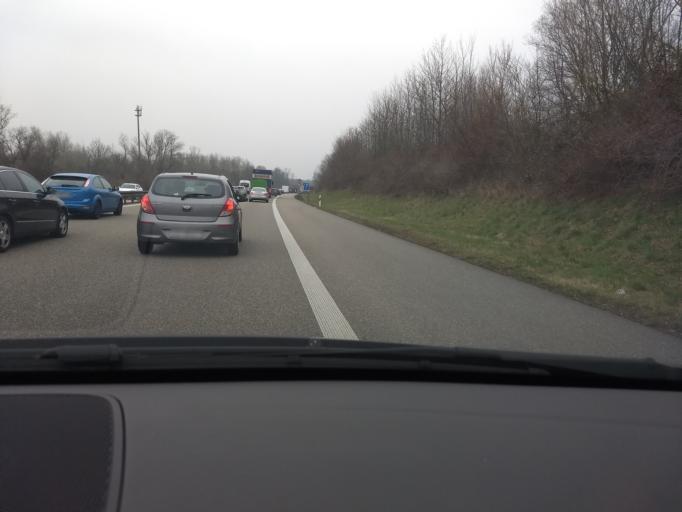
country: FR
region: Alsace
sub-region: Departement du Haut-Rhin
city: Kembs
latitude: 47.7028
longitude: 7.5225
